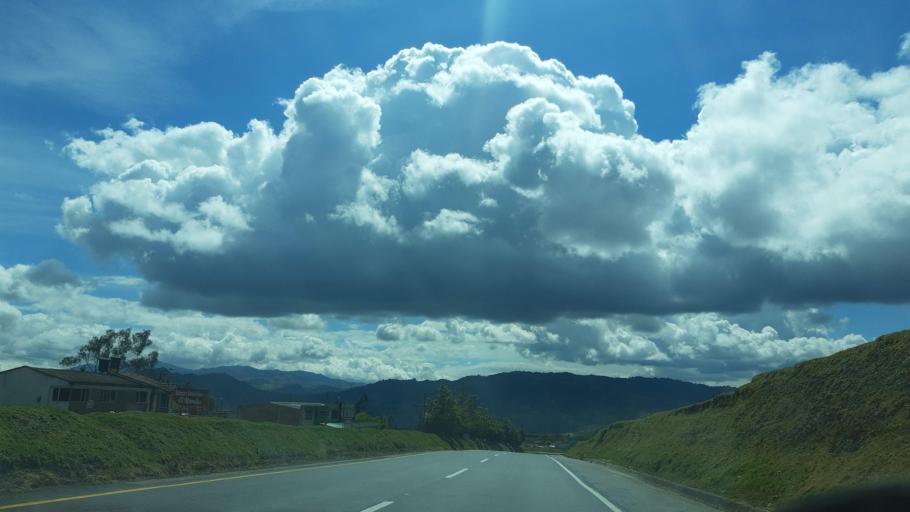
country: CO
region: Boyaca
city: Ventaquemada
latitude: 5.3838
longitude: -73.5030
